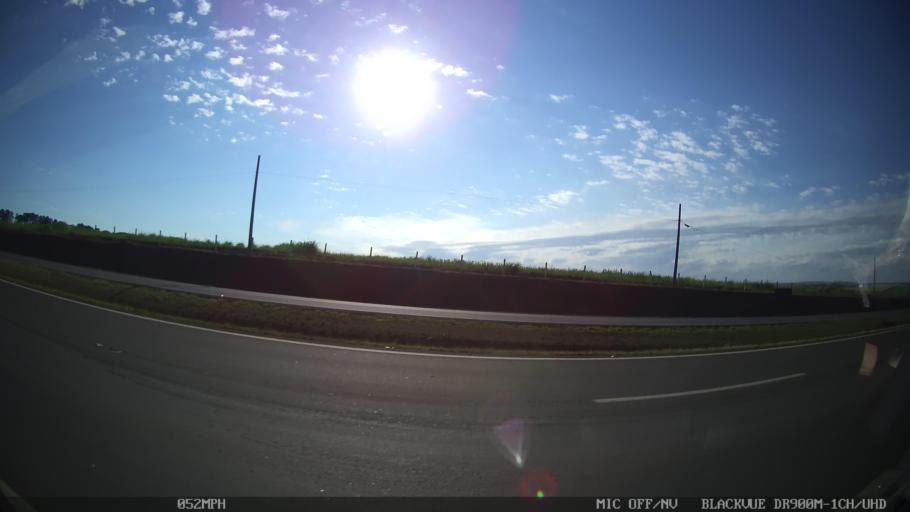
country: BR
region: Sao Paulo
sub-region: Piracicaba
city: Piracicaba
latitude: -22.6881
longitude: -47.6409
